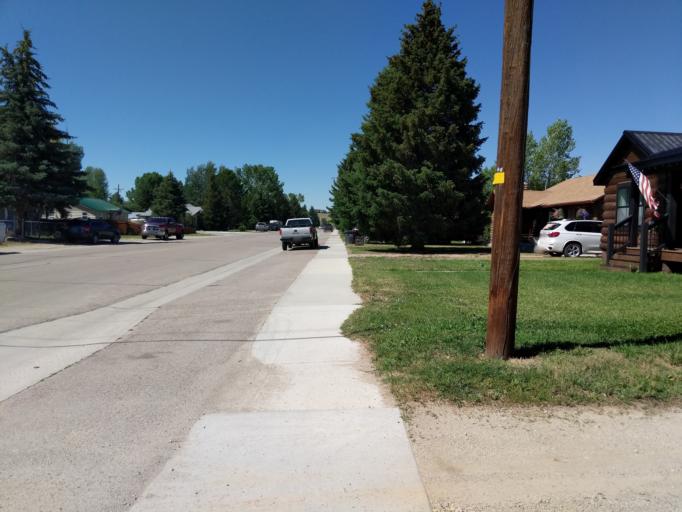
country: US
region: Wyoming
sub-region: Sublette County
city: Pinedale
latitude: 42.8680
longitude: -109.8612
